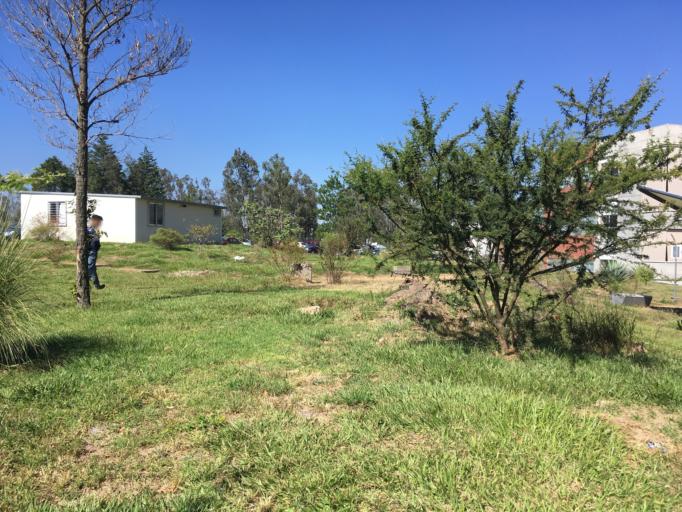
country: MX
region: Michoacan
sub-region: Morelia
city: Morelos
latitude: 19.6490
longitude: -101.2225
